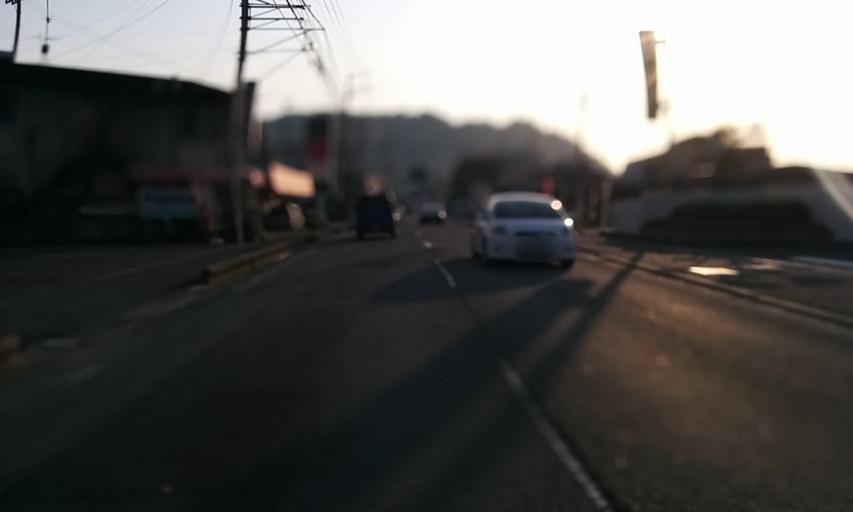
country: JP
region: Ehime
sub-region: Shikoku-chuo Shi
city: Matsuyama
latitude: 33.7820
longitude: 132.7954
